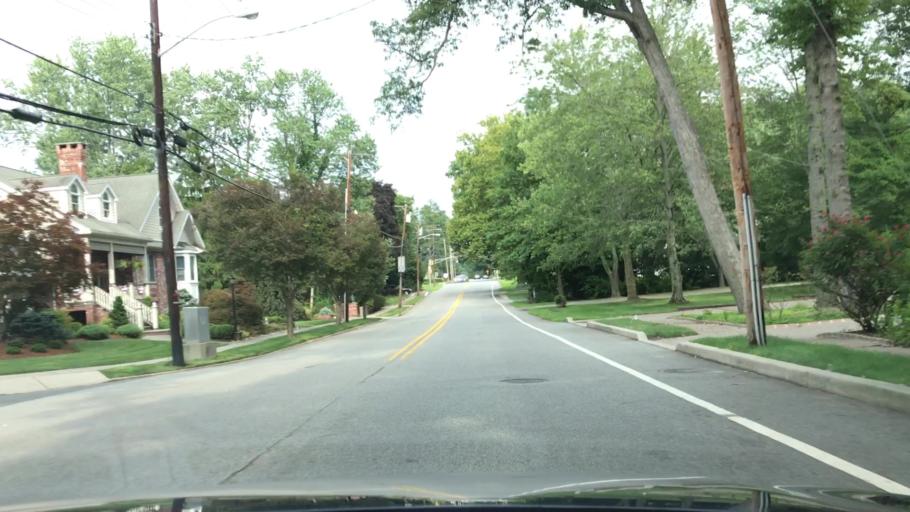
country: US
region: New Jersey
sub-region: Bergen County
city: Harrington Park
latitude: 40.9692
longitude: -73.9762
